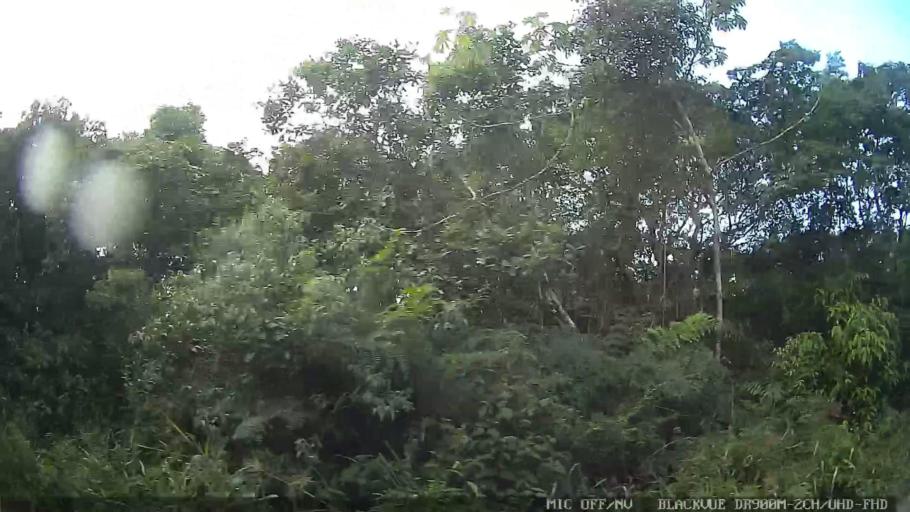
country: BR
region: Sao Paulo
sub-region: Peruibe
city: Peruibe
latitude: -24.2131
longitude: -46.9198
